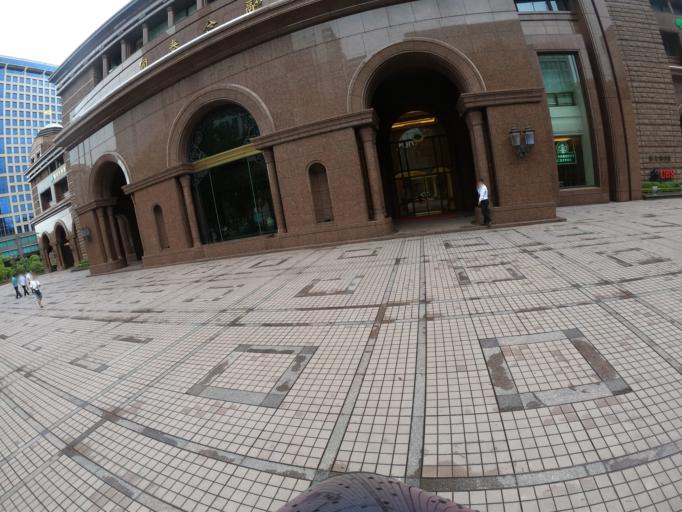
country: TW
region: Taipei
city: Taipei
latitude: 25.0382
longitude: 121.5688
